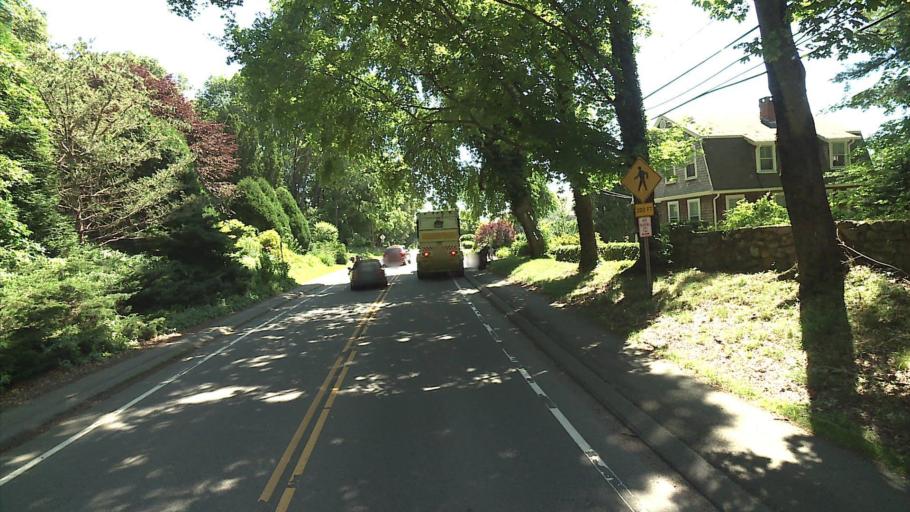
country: US
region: Connecticut
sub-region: New London County
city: Noank
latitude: 41.3407
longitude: -71.9866
